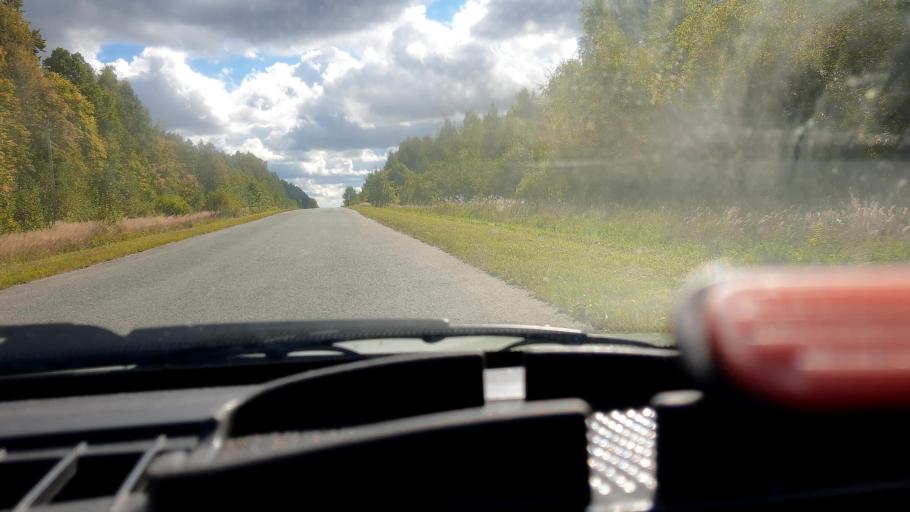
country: RU
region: Mariy-El
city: Kilemary
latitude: 56.9252
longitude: 46.7096
